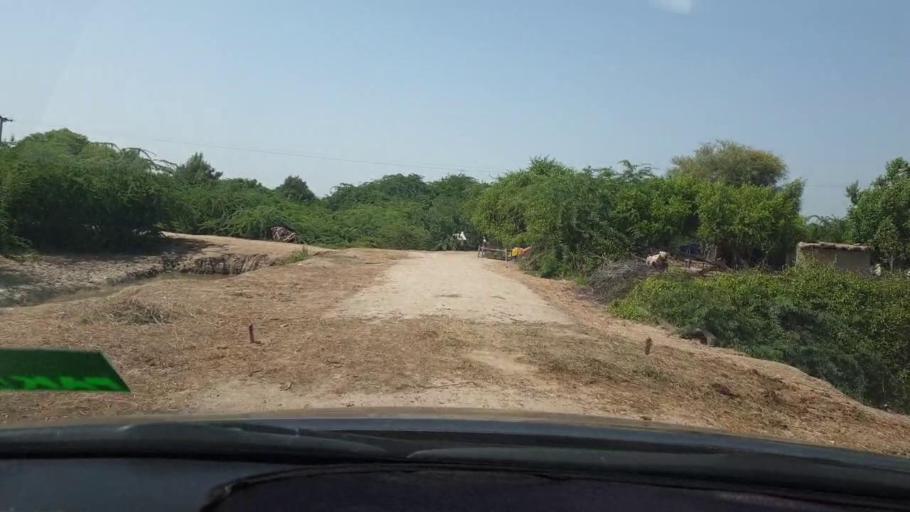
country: PK
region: Sindh
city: Digri
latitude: 24.9414
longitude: 69.1558
